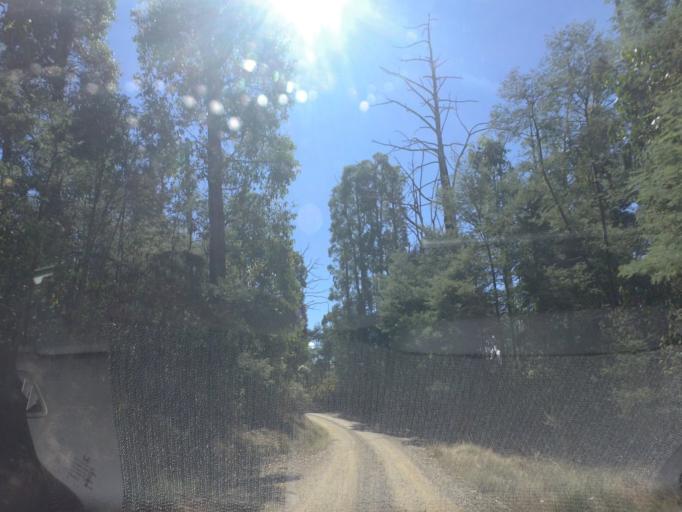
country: AU
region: Victoria
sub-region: Yarra Ranges
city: Millgrove
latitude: -37.5373
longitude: 145.7539
